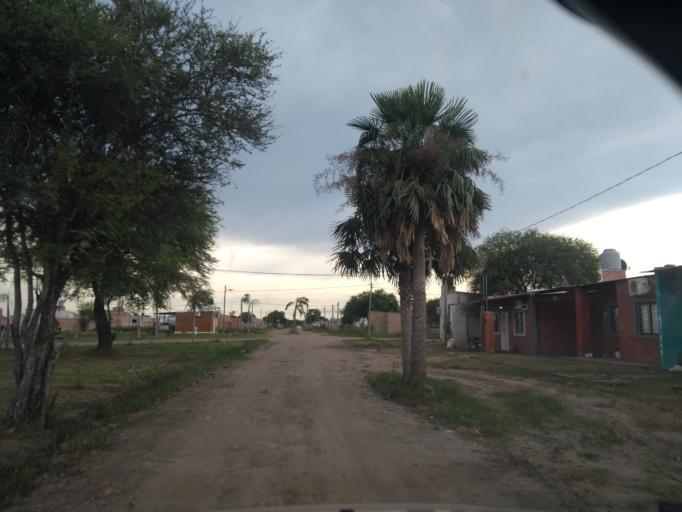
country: AR
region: Chaco
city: Resistencia
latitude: -27.4660
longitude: -59.0297
